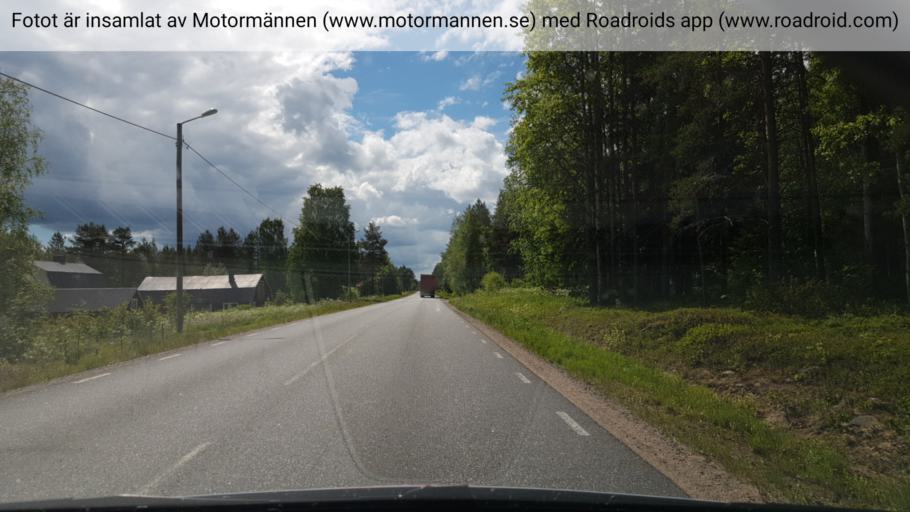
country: FI
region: Lapland
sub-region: Torniolaakso
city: Ylitornio
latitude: 66.2753
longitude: 23.6535
